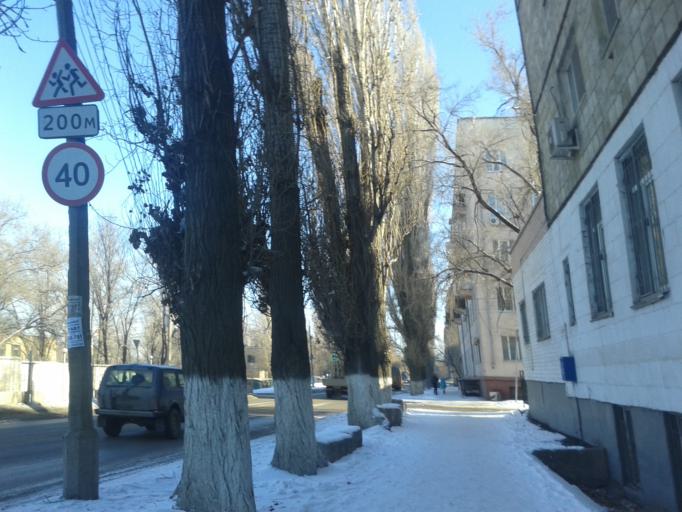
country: RU
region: Volgograd
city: Vodstroy
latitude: 48.8071
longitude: 44.5954
